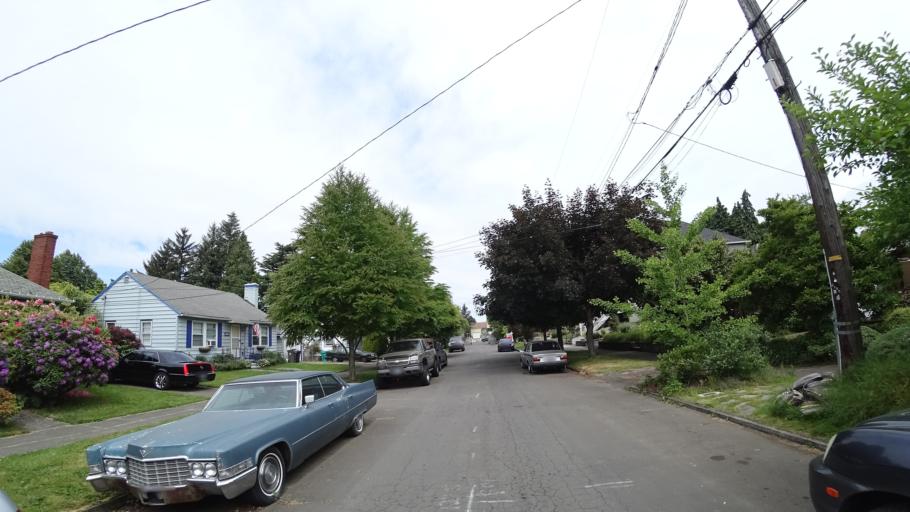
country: US
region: Oregon
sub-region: Multnomah County
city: Portland
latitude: 45.5691
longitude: -122.6287
